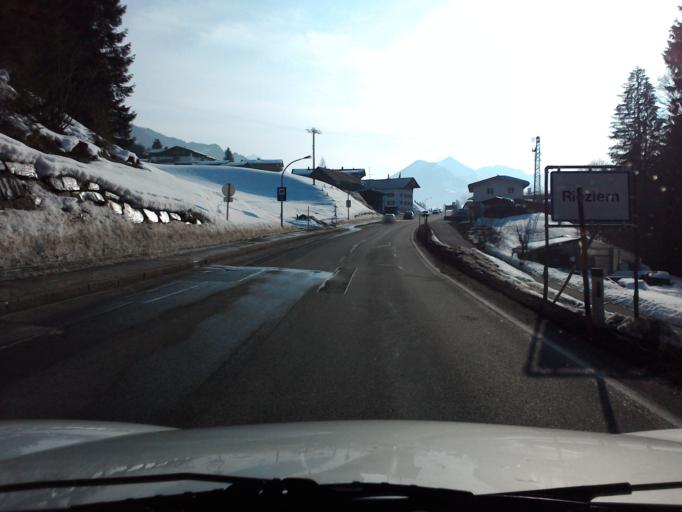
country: AT
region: Vorarlberg
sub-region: Politischer Bezirk Bregenz
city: Mittelberg
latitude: 47.3683
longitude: 10.2015
